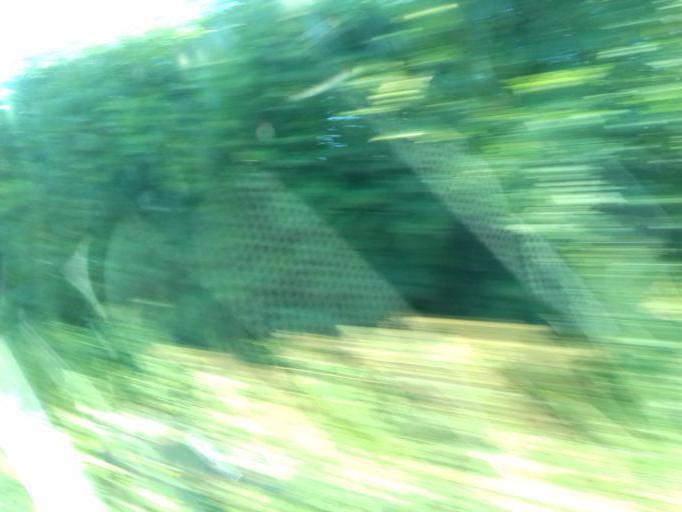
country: IE
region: Leinster
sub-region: Fingal County
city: Swords
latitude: 53.4975
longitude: -6.2863
